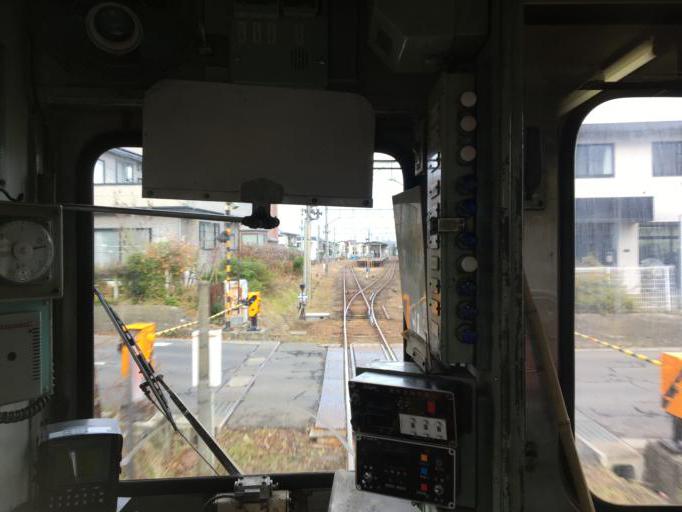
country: JP
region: Aomori
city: Hirosaki
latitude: 40.5823
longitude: 140.4710
